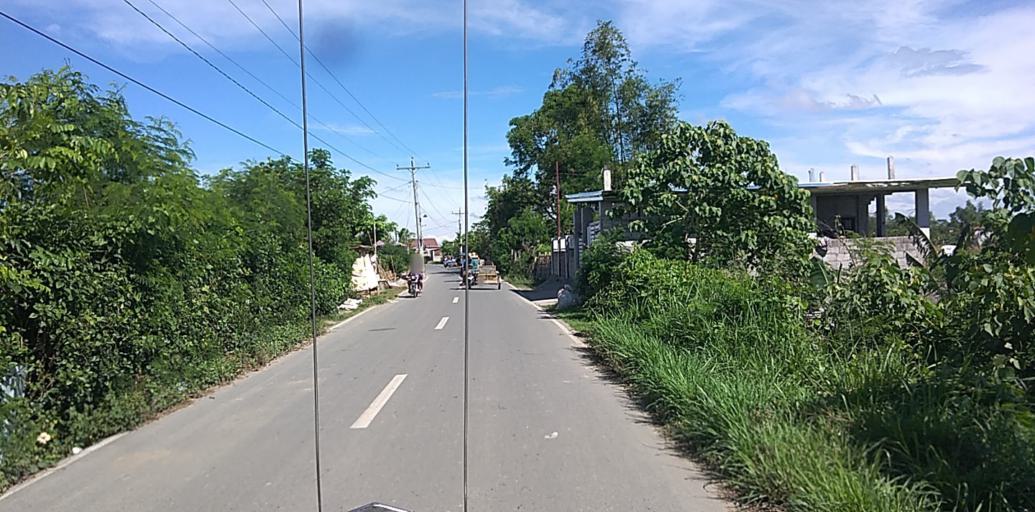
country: PH
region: Central Luzon
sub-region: Province of Pampanga
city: Candaba
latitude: 15.1078
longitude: 120.8164
